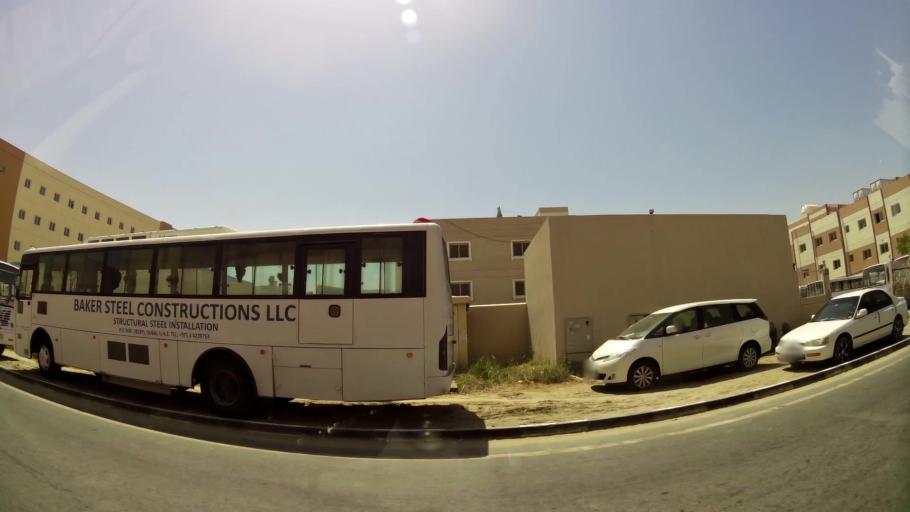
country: AE
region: Dubai
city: Dubai
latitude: 24.9778
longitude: 55.1584
